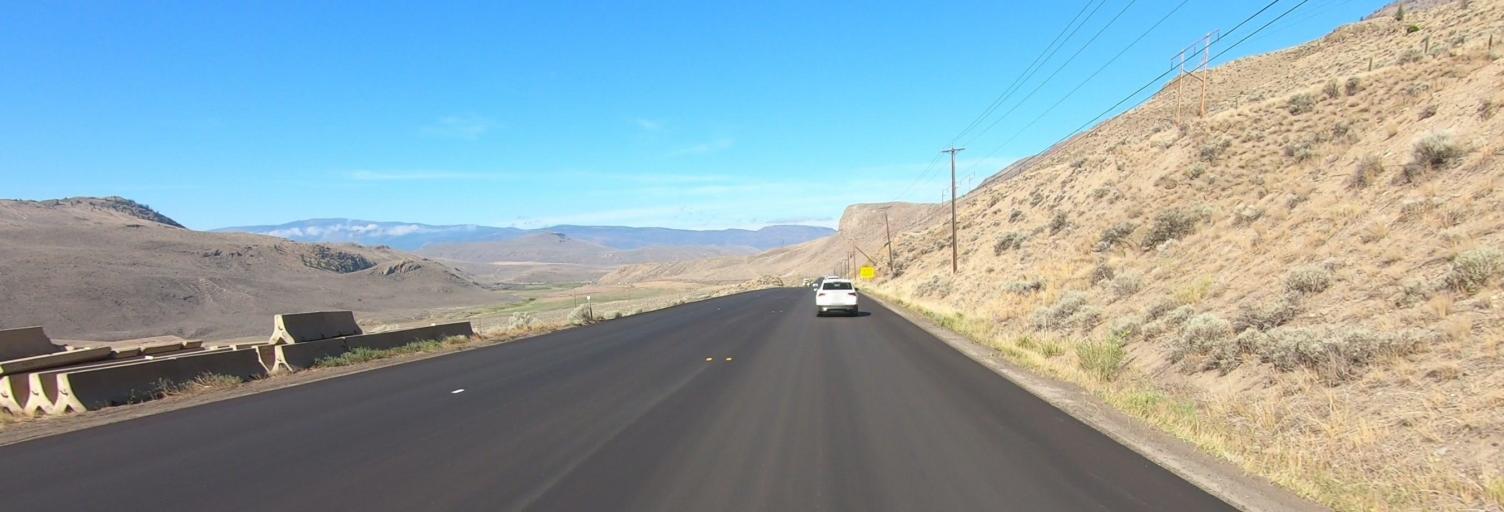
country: CA
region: British Columbia
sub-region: Thompson-Nicola Regional District
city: Ashcroft
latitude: 50.7897
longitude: -121.1519
